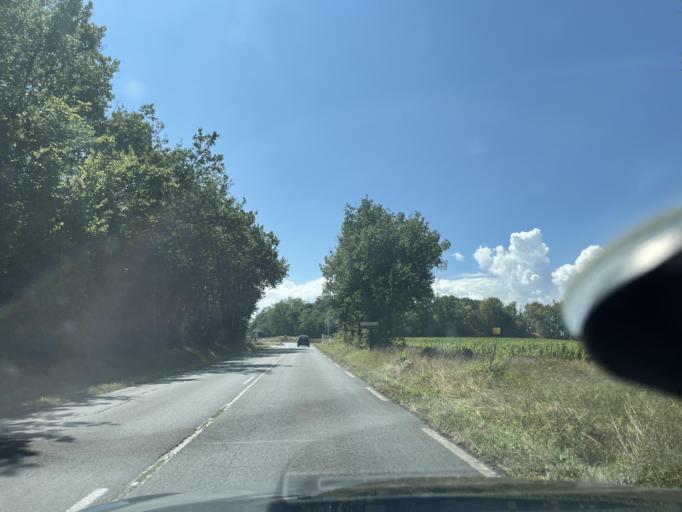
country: FR
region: Aquitaine
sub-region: Departement de la Gironde
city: Cars
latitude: 45.0913
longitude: -0.6391
